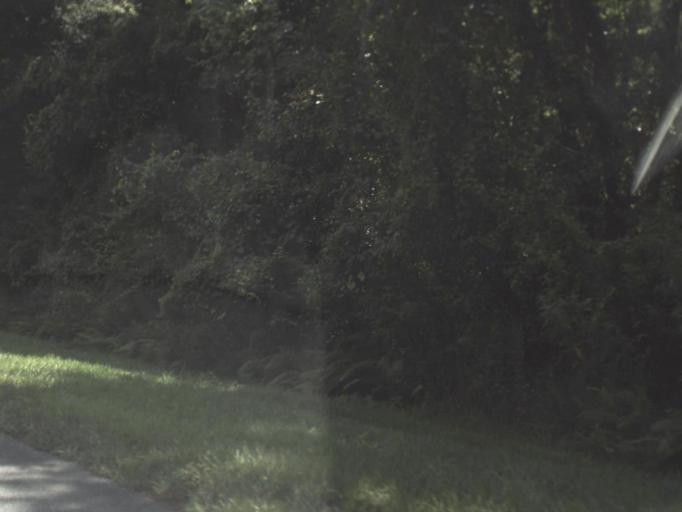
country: US
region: Florida
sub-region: Hernando County
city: Ridge Manor
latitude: 28.5193
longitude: -82.1010
